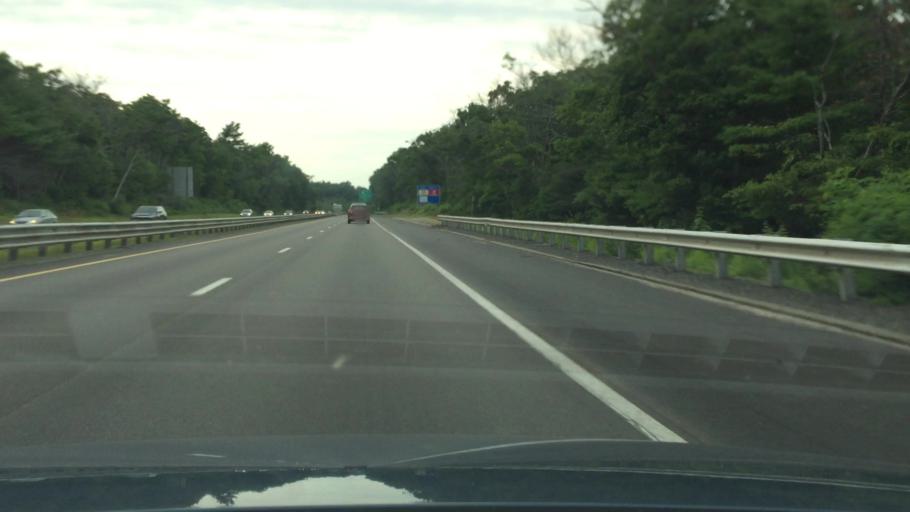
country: US
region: Massachusetts
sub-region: Plymouth County
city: Plymouth
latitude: 41.9404
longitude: -70.6693
